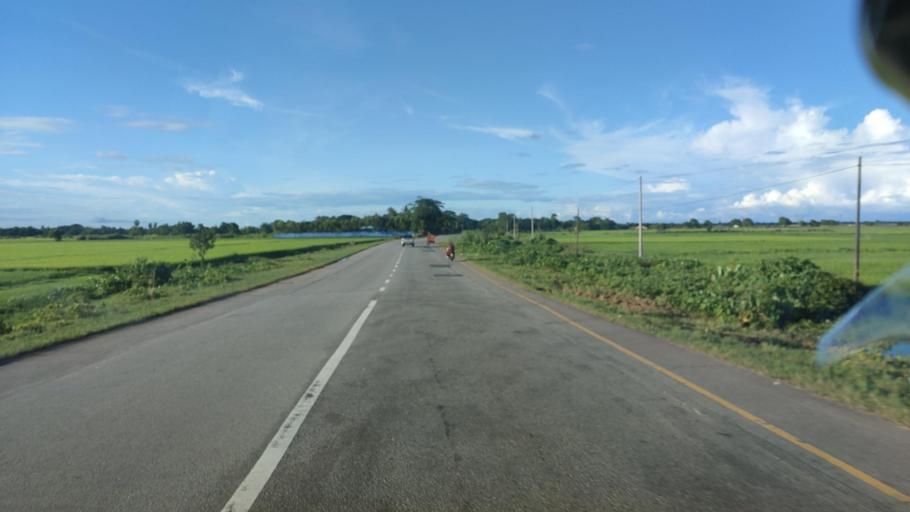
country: MM
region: Bago
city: Nyaunglebin
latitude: 17.6989
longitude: 96.5896
